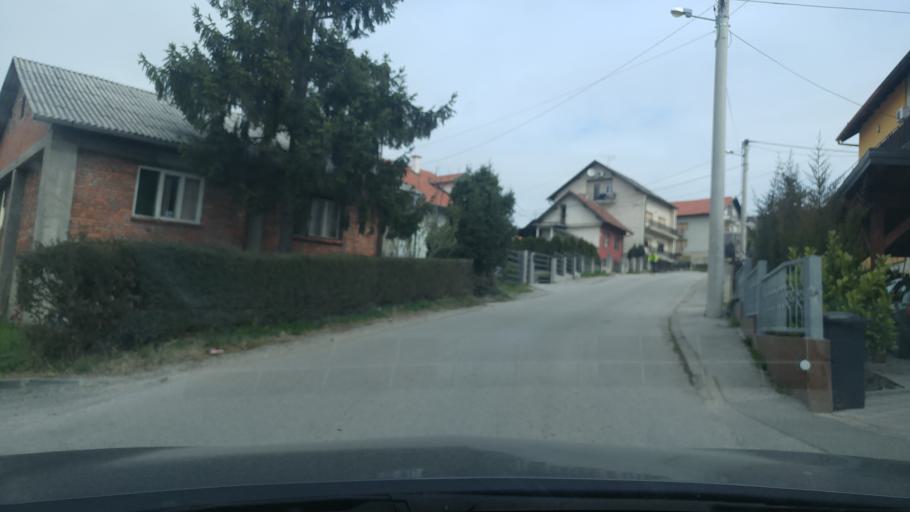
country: HR
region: Grad Zagreb
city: Stenjevec
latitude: 45.8389
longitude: 15.9226
